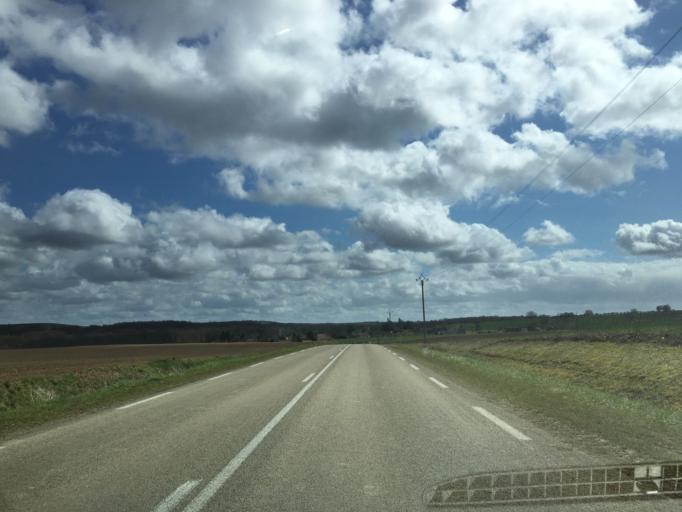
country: FR
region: Bourgogne
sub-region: Departement de l'Yonne
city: Aillant-sur-Tholon
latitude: 47.8474
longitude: 3.3850
